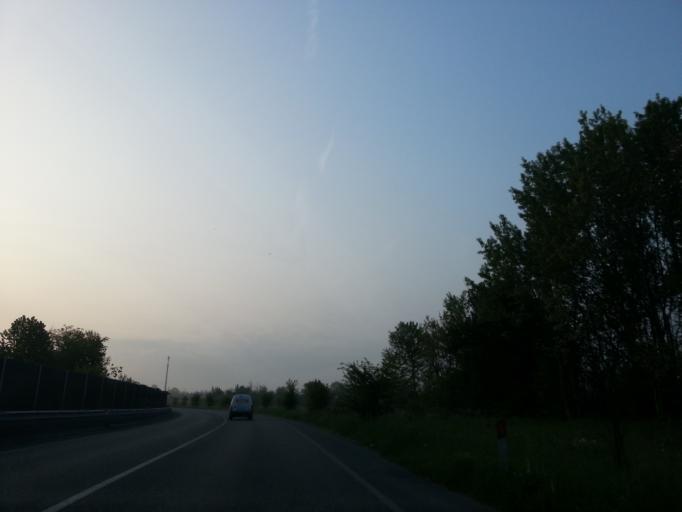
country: IT
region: Emilia-Romagna
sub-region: Provincia di Reggio Emilia
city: Albinea
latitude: 44.6657
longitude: 10.6058
